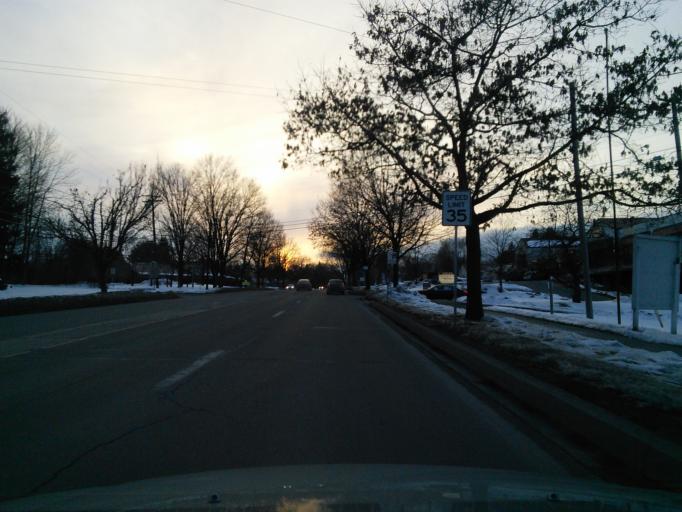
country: US
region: Pennsylvania
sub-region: Centre County
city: State College
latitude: 40.7848
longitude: -77.8413
